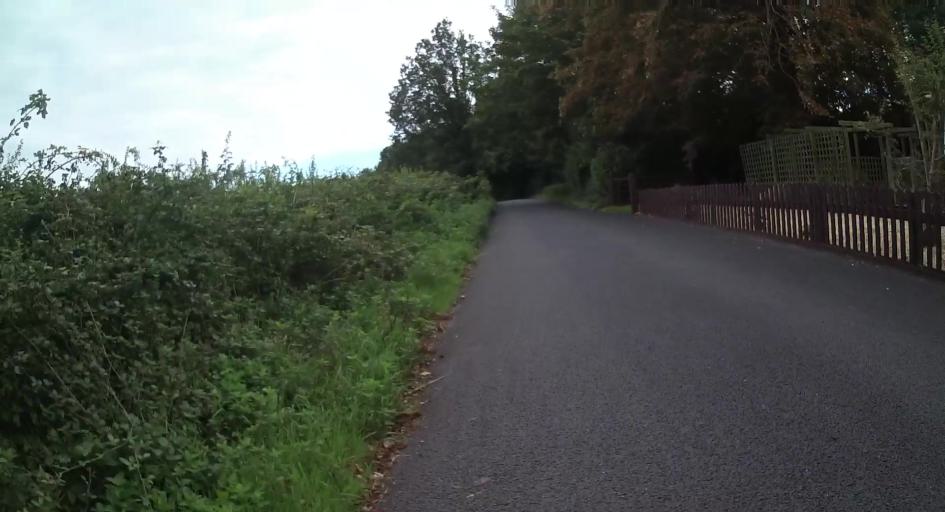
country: GB
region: England
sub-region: Isle of Wight
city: Freshwater
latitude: 50.6813
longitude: -1.5068
